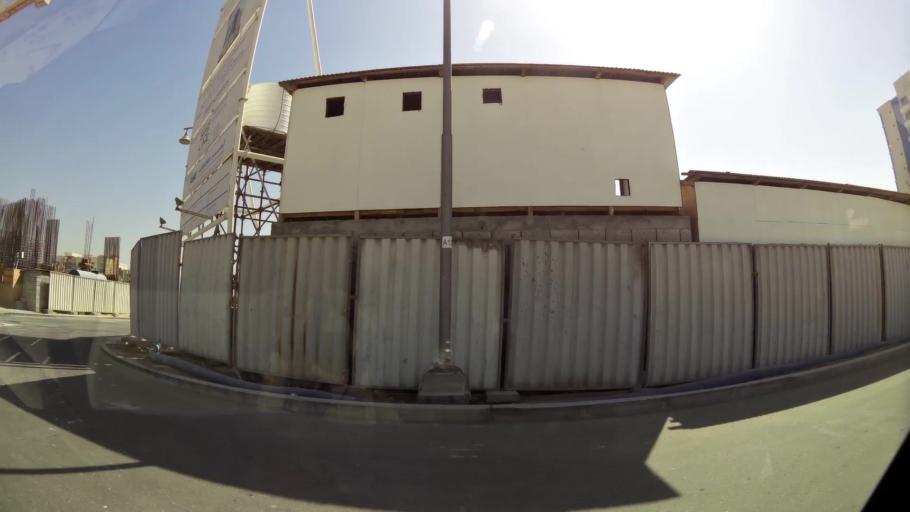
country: AE
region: Dubai
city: Dubai
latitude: 25.0387
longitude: 55.1396
